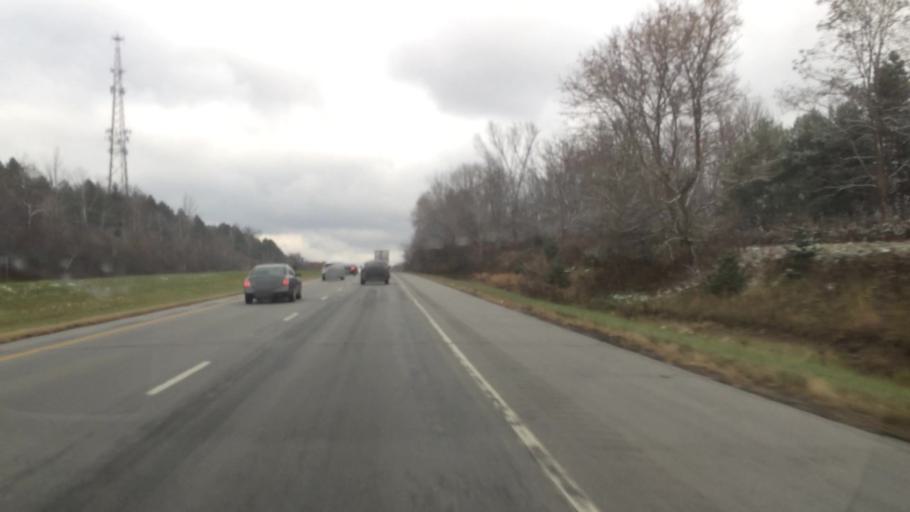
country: US
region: Ohio
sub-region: Summit County
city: Hudson
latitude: 41.2742
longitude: -81.4064
